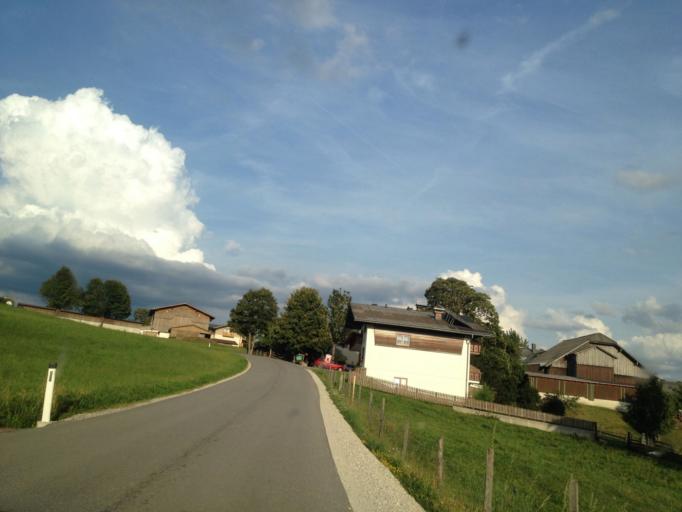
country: AT
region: Styria
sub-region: Politischer Bezirk Liezen
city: Schladming
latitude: 47.3990
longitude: 13.6172
